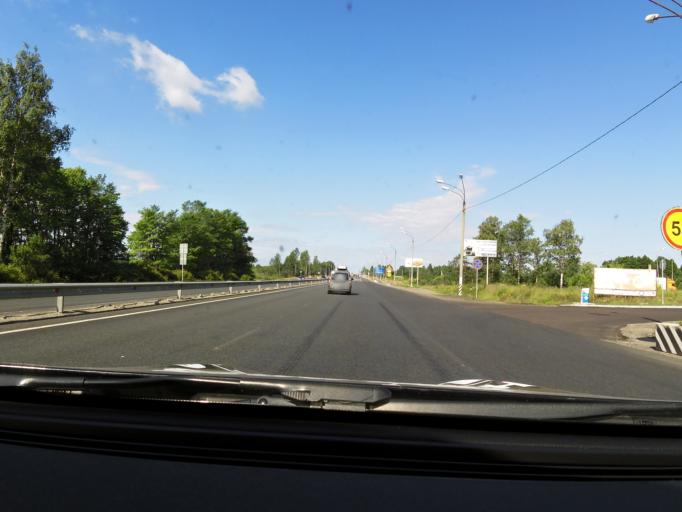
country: RU
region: Tverskaya
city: Emmaus
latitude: 56.7837
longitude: 36.0524
